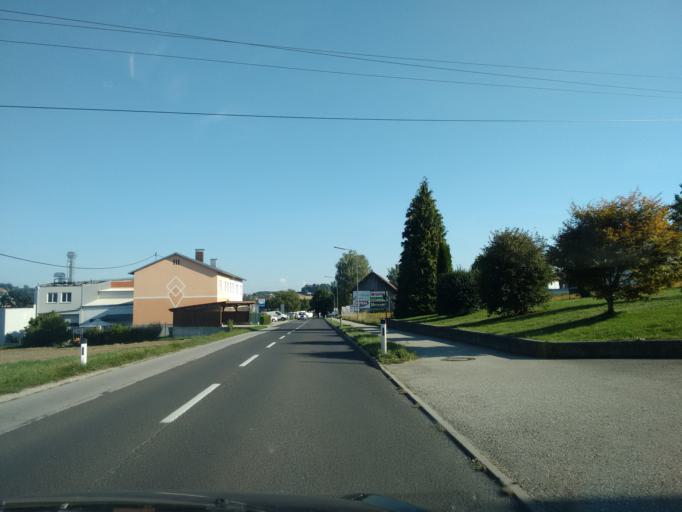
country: AT
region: Upper Austria
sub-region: Politischer Bezirk Linz-Land
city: Traun
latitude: 48.1424
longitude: 14.2265
